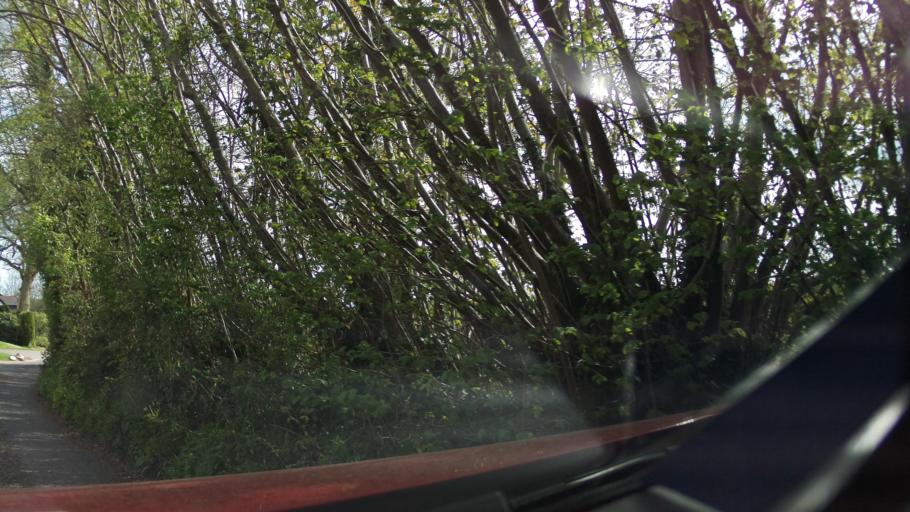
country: GB
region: England
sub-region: Hampshire
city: Romsey
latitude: 51.0343
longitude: -1.5077
